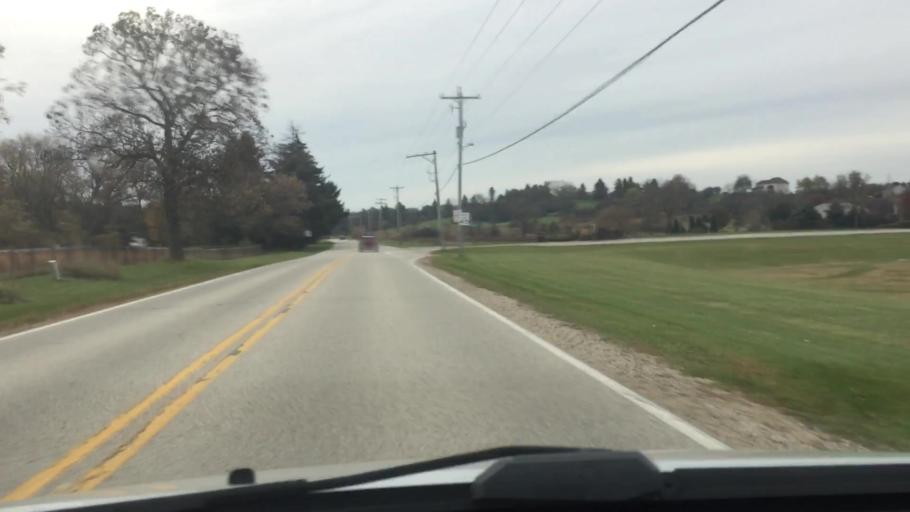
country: US
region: Wisconsin
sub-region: Waukesha County
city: Mukwonago
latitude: 42.8875
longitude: -88.3772
